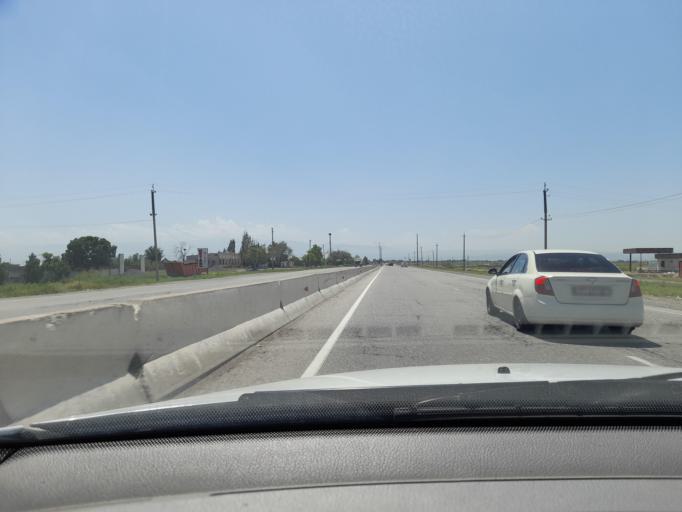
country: UZ
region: Jizzax
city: Paxtakor
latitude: 40.1792
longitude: 67.9668
